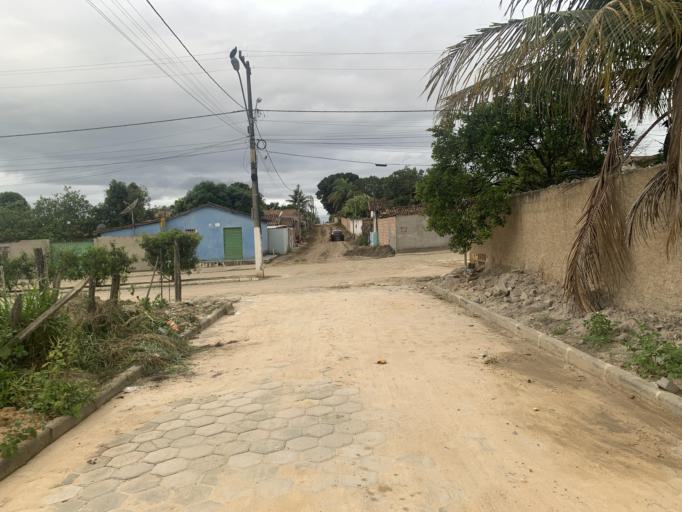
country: BR
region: Bahia
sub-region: Medeiros Neto
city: Medeiros Neto
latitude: -17.3908
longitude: -40.2315
